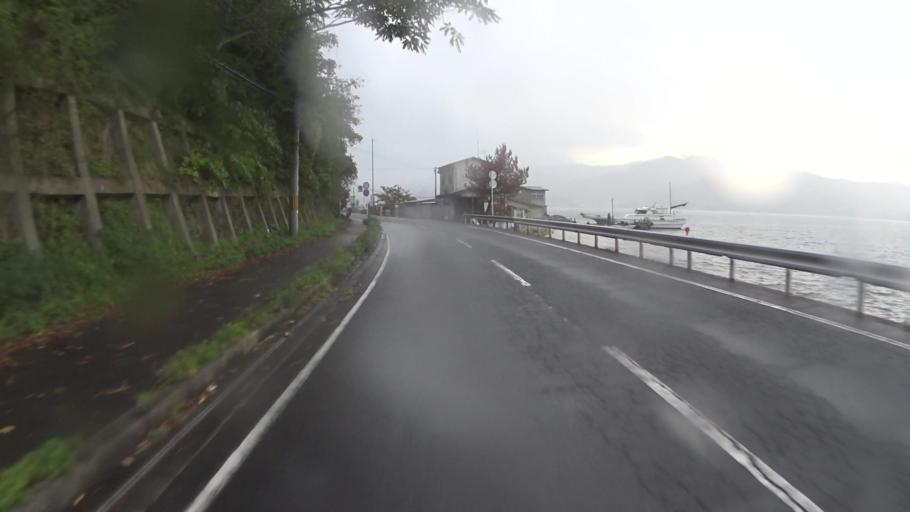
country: JP
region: Kyoto
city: Miyazu
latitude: 35.5609
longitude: 135.2055
